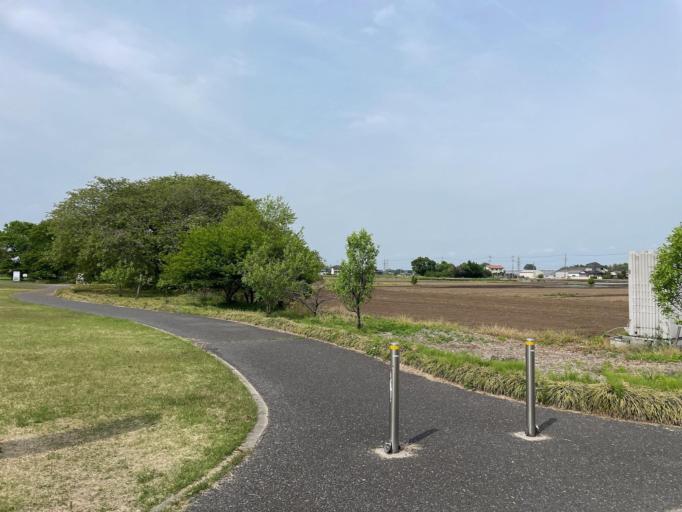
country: JP
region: Tochigi
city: Mibu
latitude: 36.3844
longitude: 139.8121
